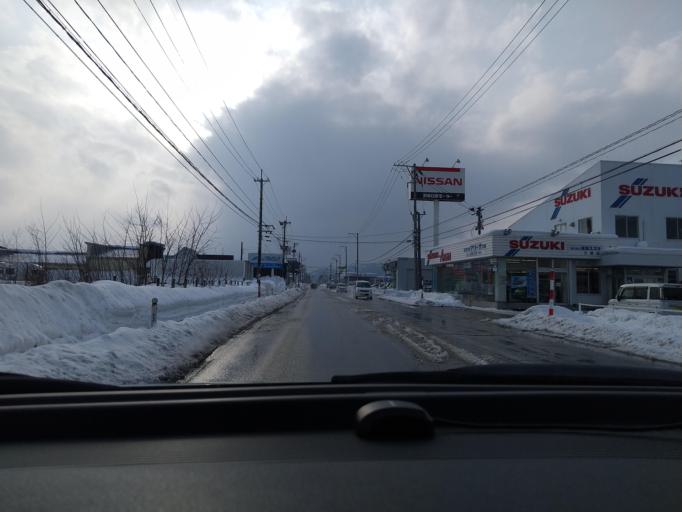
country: JP
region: Akita
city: Omagari
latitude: 39.4870
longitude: 140.4927
